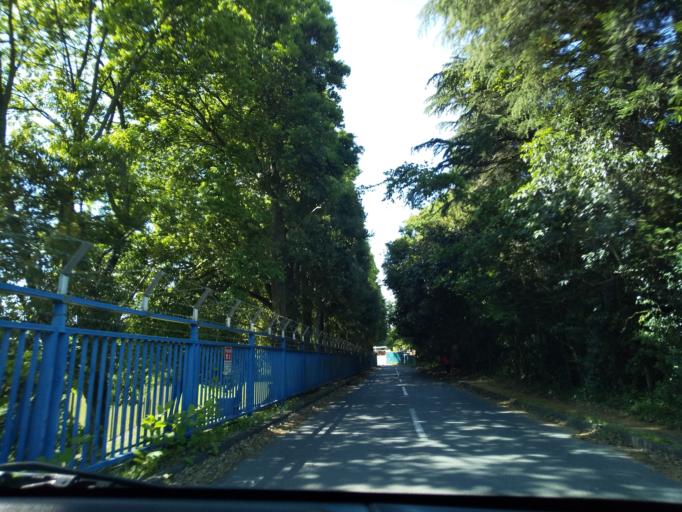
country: JP
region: Kanagawa
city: Zama
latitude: 35.5432
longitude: 139.3896
